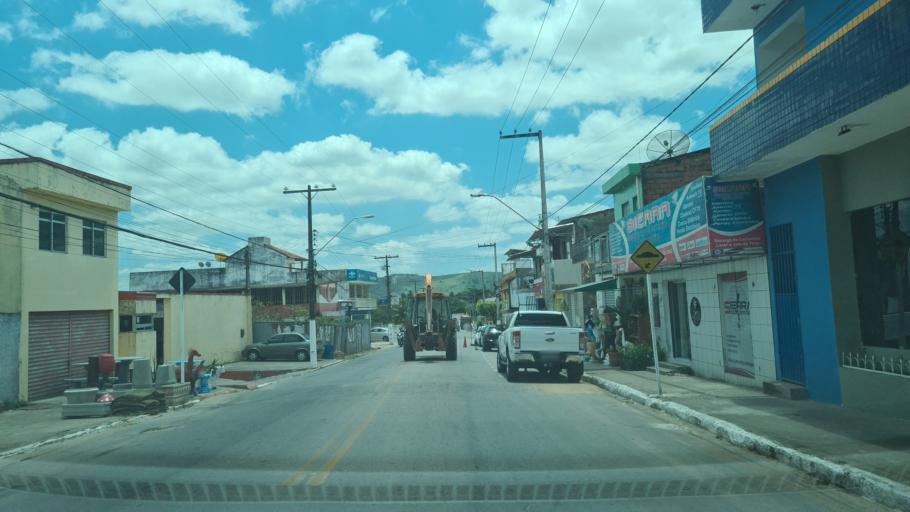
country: BR
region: Alagoas
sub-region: Uniao Dos Palmares
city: Uniao dos Palmares
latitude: -9.1652
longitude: -36.0239
